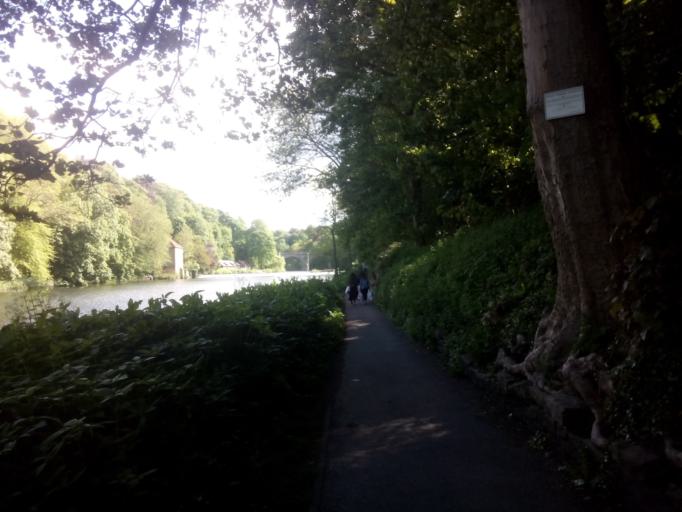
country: GB
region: England
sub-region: County Durham
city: Durham
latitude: 54.7748
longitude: -1.5787
